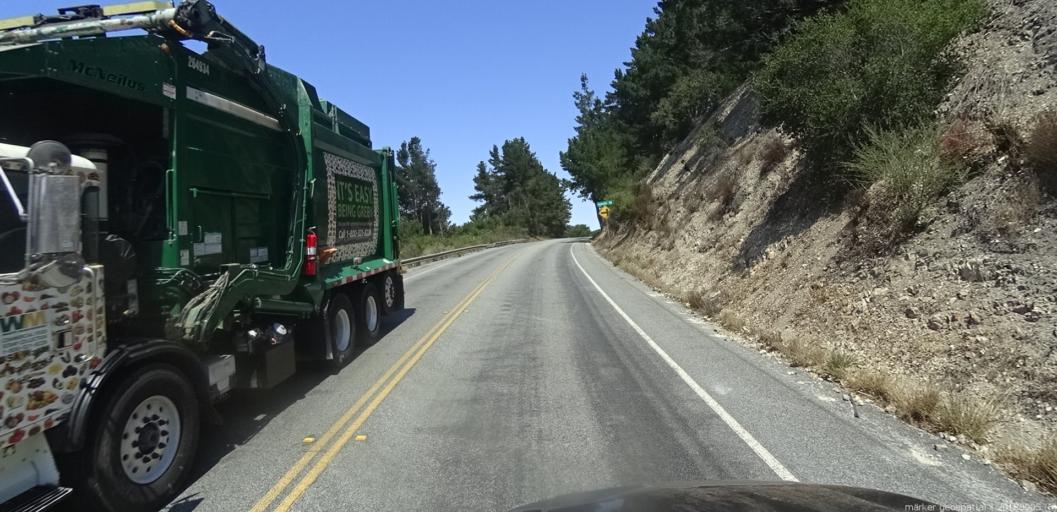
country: US
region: California
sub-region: Monterey County
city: Carmel Valley Village
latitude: 36.5398
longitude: -121.7536
